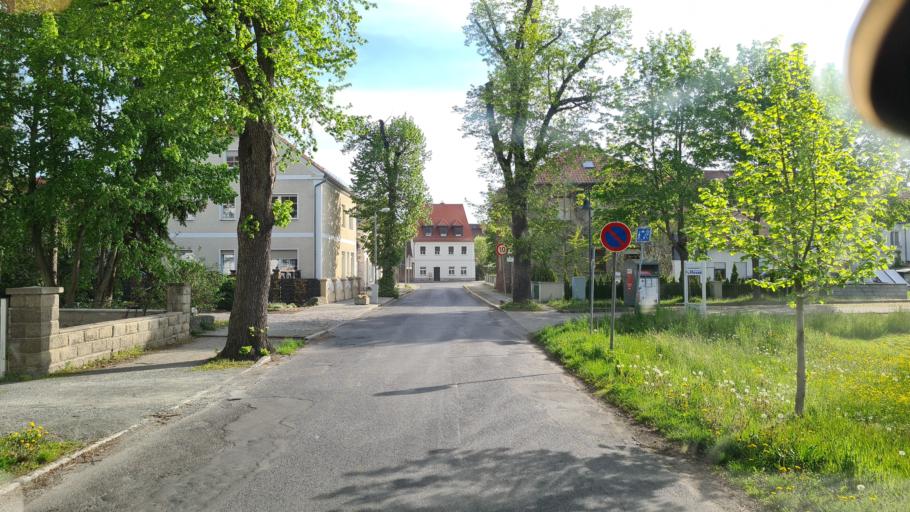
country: DE
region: Brandenburg
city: Ortrand
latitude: 51.3756
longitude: 13.7553
